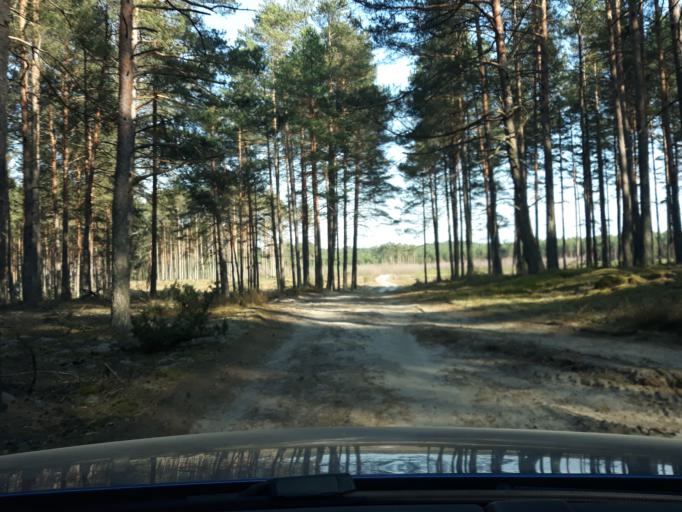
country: PL
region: Pomeranian Voivodeship
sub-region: Powiat bytowski
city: Lipnica
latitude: 53.9176
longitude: 17.4688
